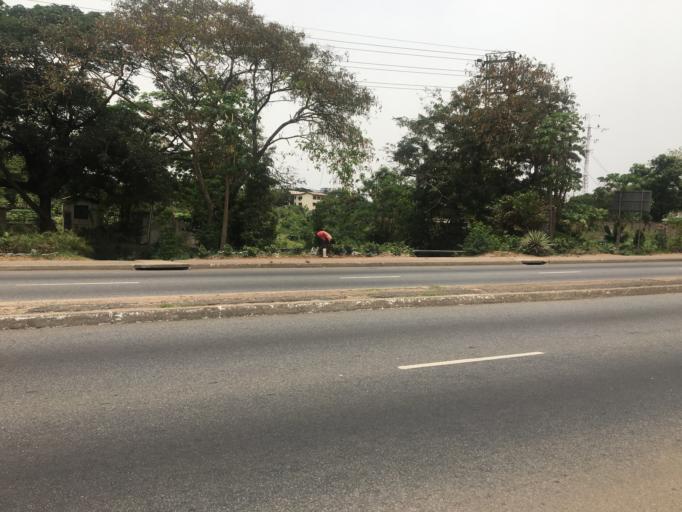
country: GH
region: Greater Accra
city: Accra
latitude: 5.5943
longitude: -0.1876
